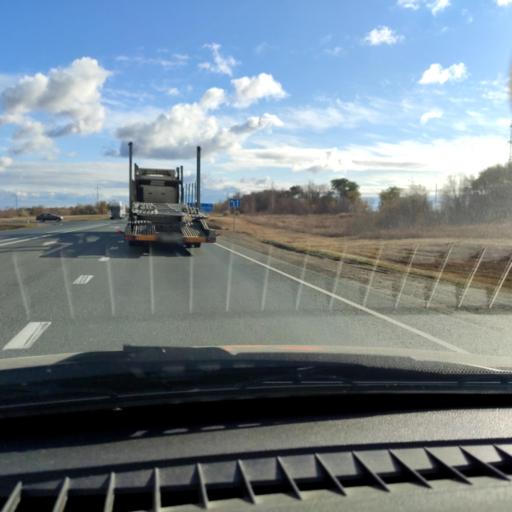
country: RU
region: Samara
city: Varlamovo
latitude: 53.1949
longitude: 48.3230
